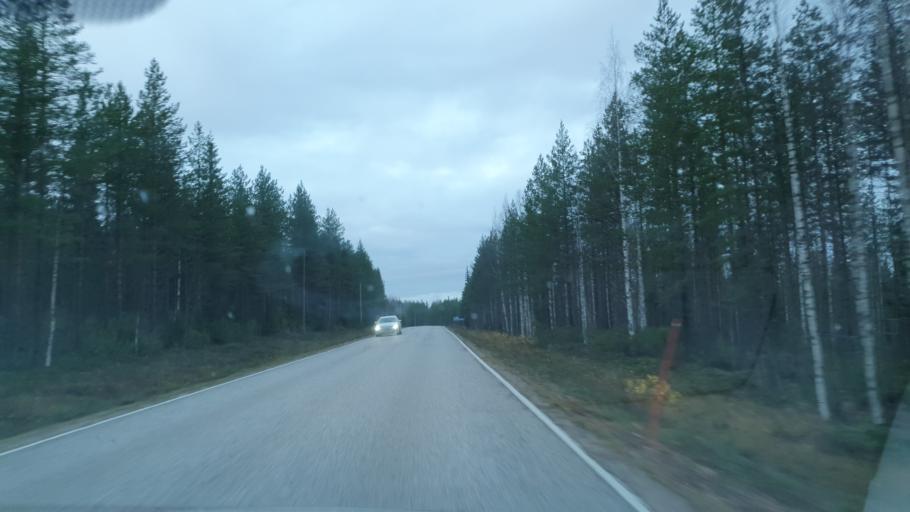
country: FI
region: Kainuu
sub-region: Kajaani
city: Ristijaervi
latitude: 64.4334
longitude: 28.3684
